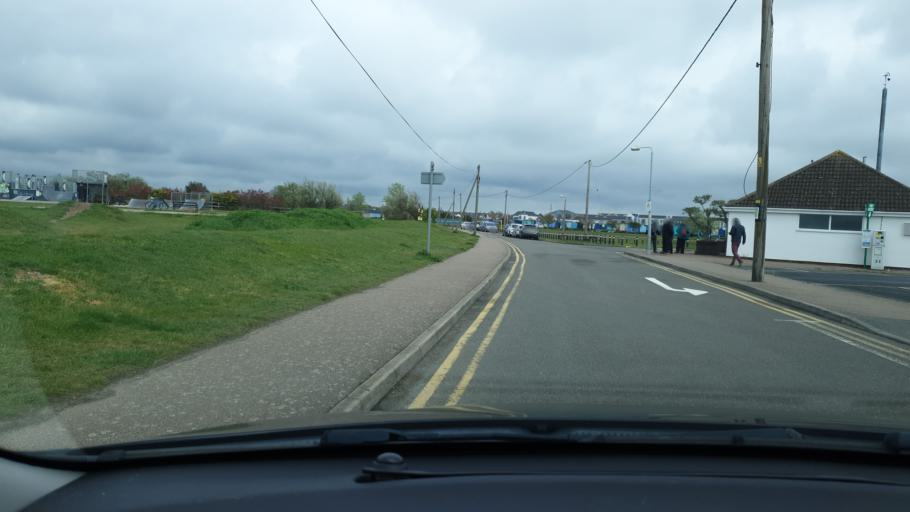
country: GB
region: England
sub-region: Essex
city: Brightlingsea
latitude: 51.8064
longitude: 1.0127
